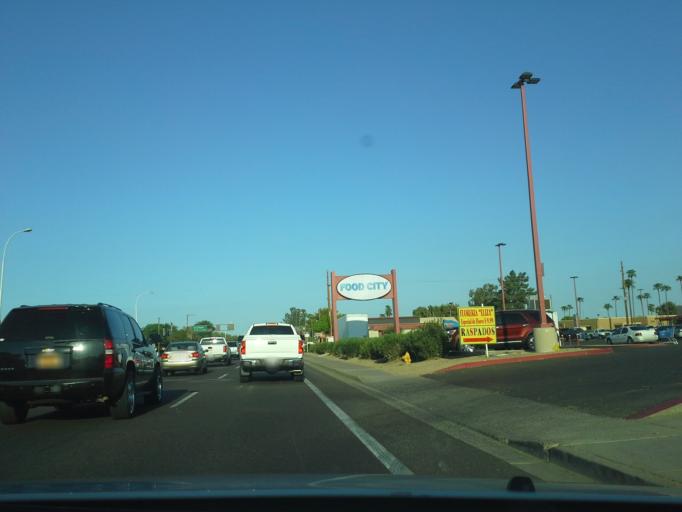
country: US
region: Arizona
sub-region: Maricopa County
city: Guadalupe
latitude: 33.3927
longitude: -111.9802
